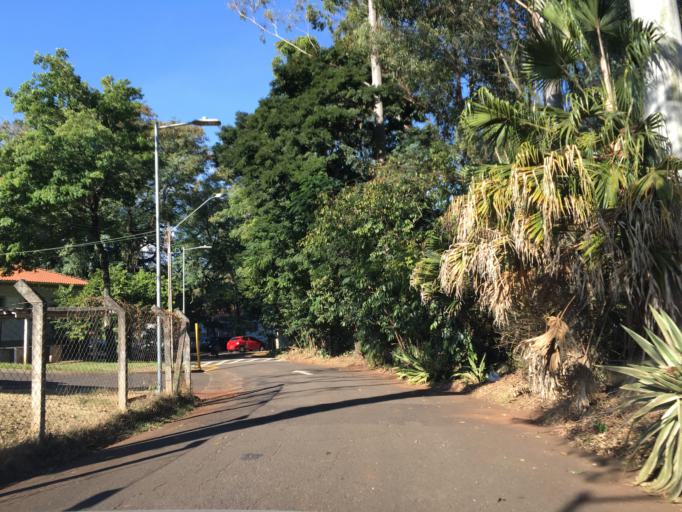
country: BR
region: Sao Paulo
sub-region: Piracicaba
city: Piracicaba
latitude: -22.7140
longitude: -47.6278
